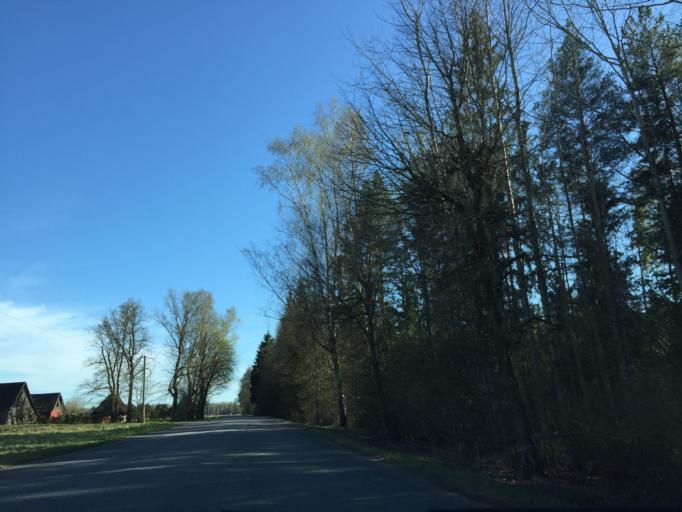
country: EE
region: Valgamaa
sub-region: Valga linn
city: Valga
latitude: 57.8605
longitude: 26.2530
